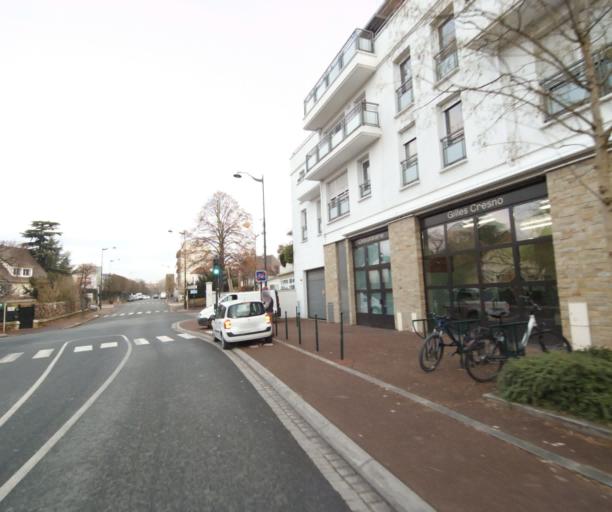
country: FR
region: Ile-de-France
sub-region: Departement des Hauts-de-Seine
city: Rueil-Malmaison
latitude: 48.8686
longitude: 2.2037
